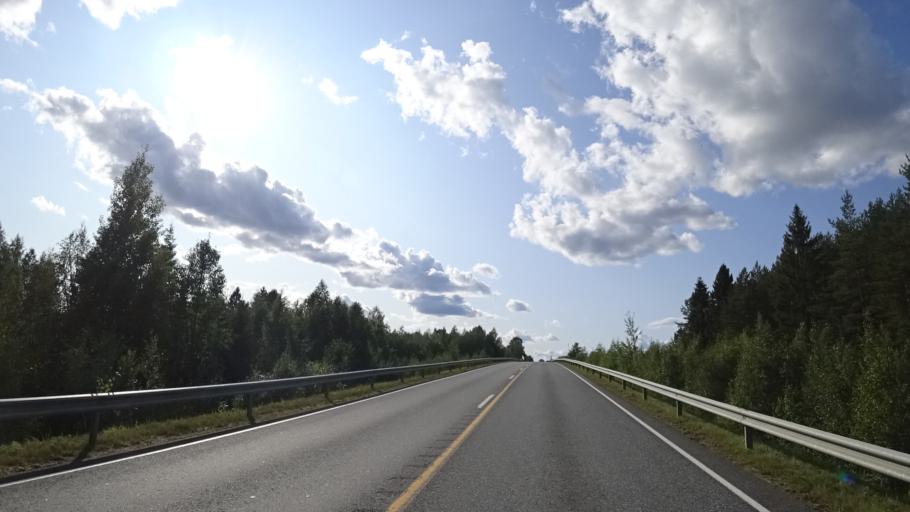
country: FI
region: North Karelia
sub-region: Keski-Karjala
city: Kitee
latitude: 62.0892
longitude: 29.9811
